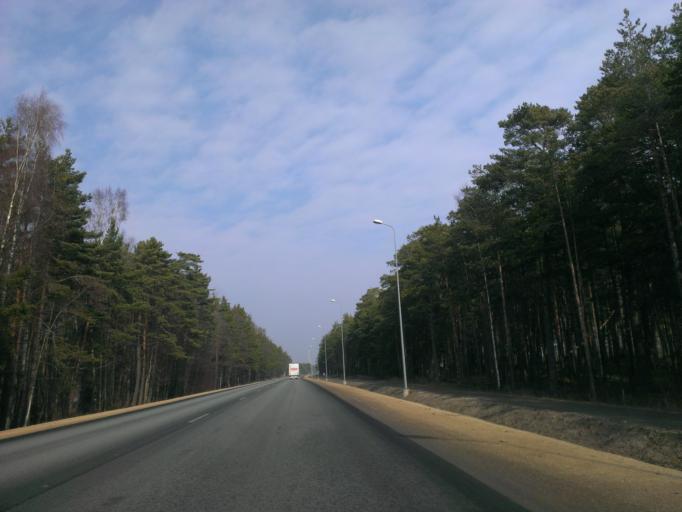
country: LV
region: Salacgrivas
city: Salacgriva
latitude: 57.7746
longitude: 24.3554
